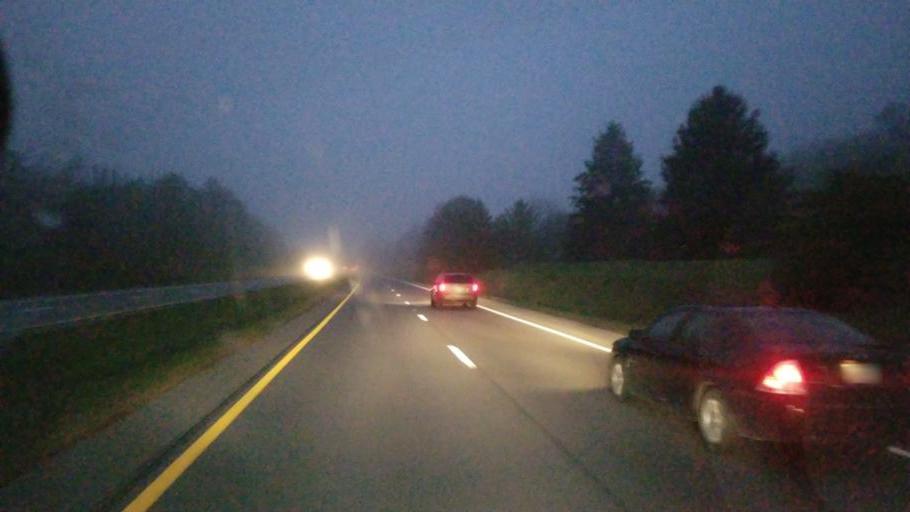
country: US
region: Ohio
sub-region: Ross County
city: Chillicothe
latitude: 39.2753
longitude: -82.9611
